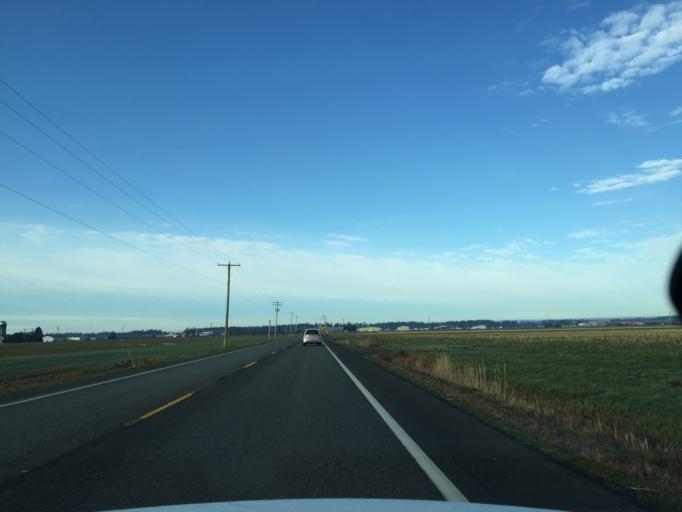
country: US
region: Washington
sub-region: Whatcom County
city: Lynden
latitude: 48.9646
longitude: -122.4683
